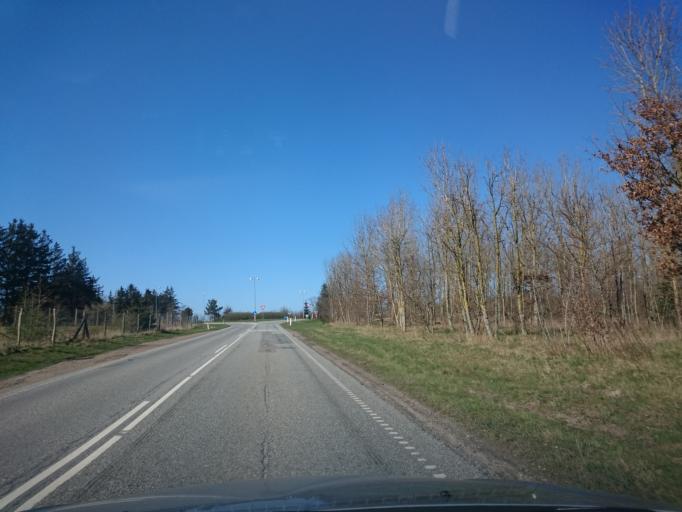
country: DK
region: North Denmark
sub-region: Hjorring Kommune
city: Hjorring
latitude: 57.5114
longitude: 10.0045
